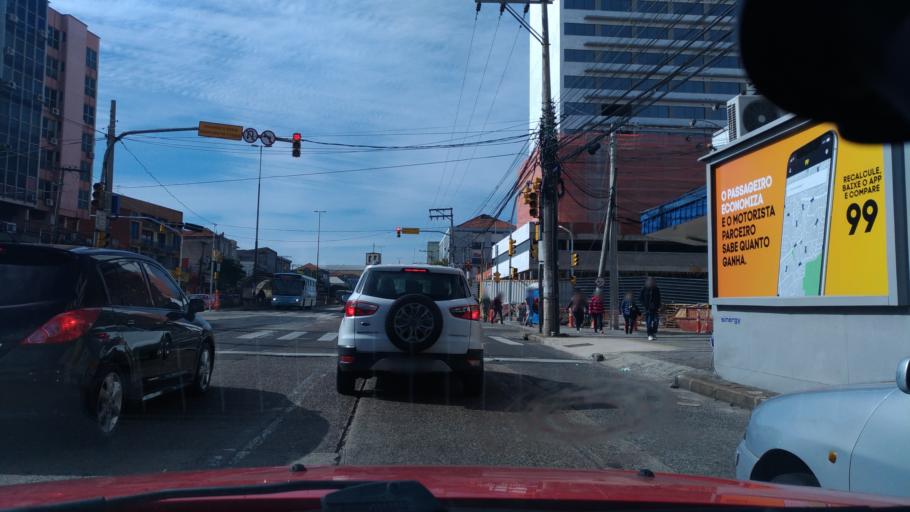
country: BR
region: Rio Grande do Sul
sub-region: Porto Alegre
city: Porto Alegre
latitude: -30.0107
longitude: -51.1597
